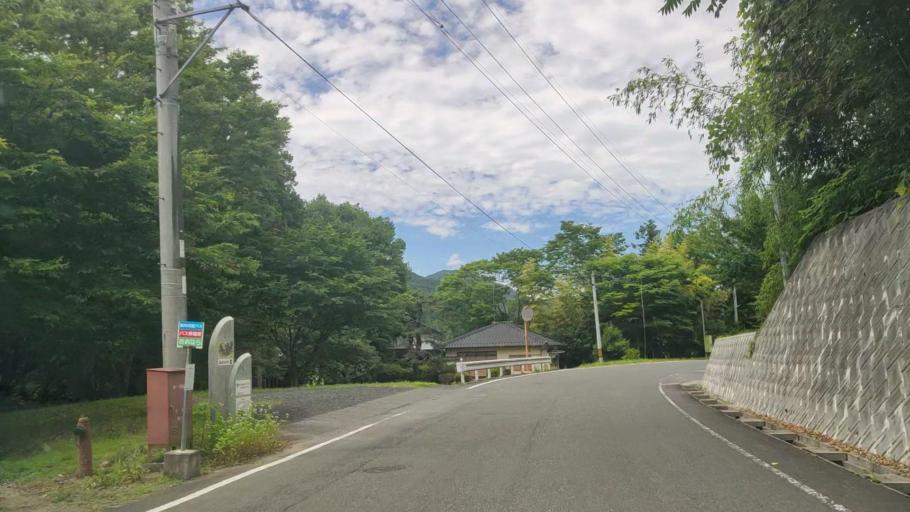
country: JP
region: Hyogo
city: Yamazakicho-nakabirose
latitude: 35.1026
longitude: 134.3292
